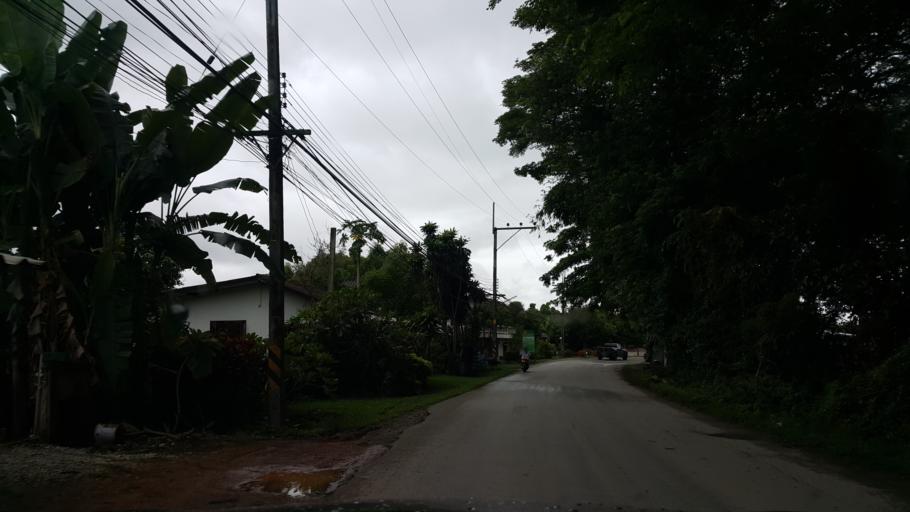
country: TH
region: Phayao
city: Chiang Kham
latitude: 19.5269
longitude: 100.3187
